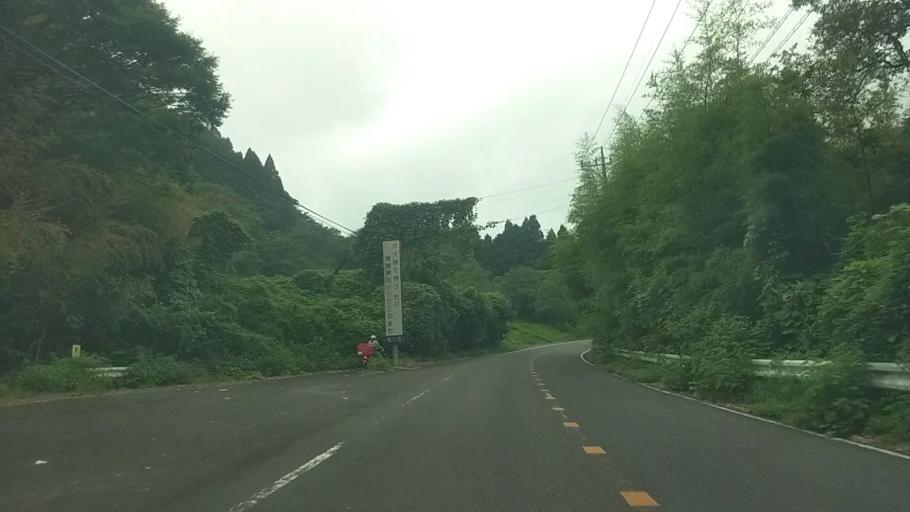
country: JP
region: Chiba
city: Kawaguchi
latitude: 35.1415
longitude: 139.9463
